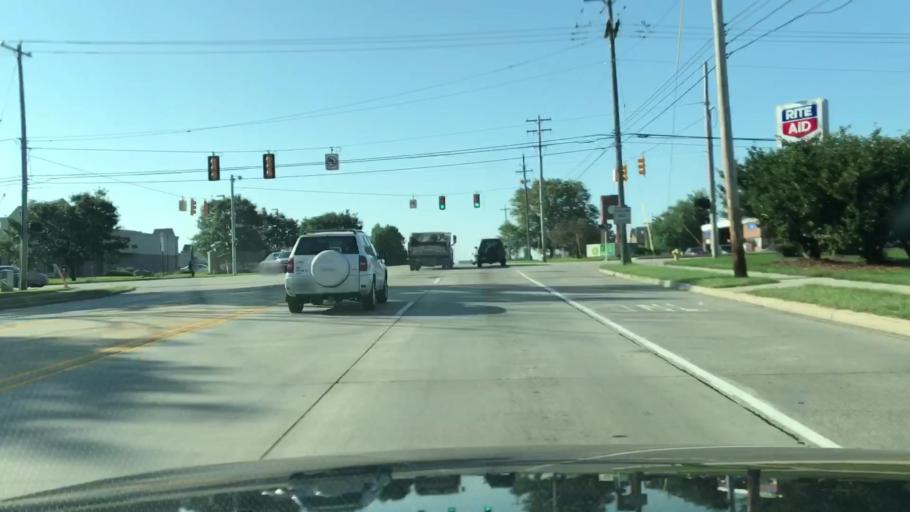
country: US
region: Michigan
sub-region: Kent County
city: Kentwood
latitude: 42.8552
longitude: -85.6250
